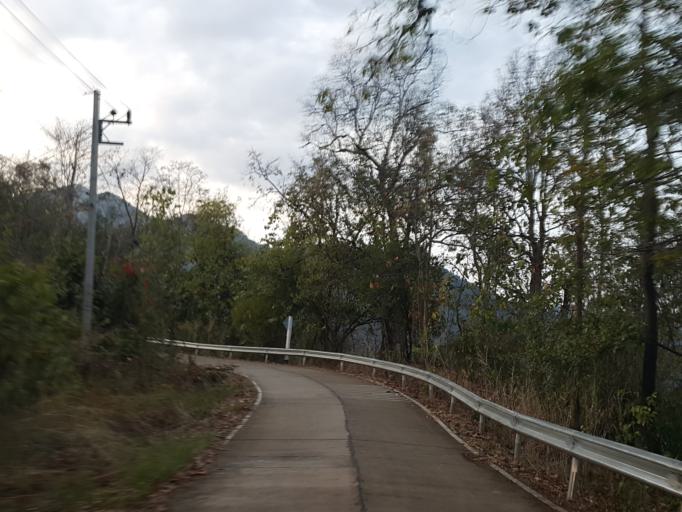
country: TH
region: Lampang
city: Mueang Pan
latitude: 18.8165
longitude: 99.4727
